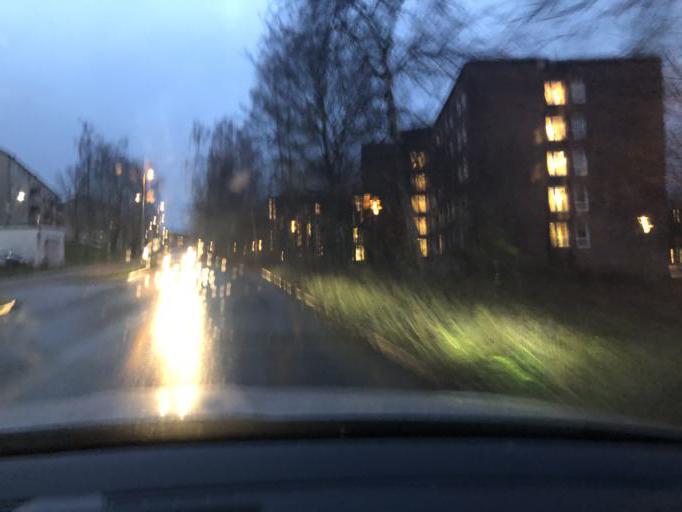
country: SE
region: Vaermland
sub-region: Karlstads Kommun
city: Karlstad
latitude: 59.3772
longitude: 13.4821
